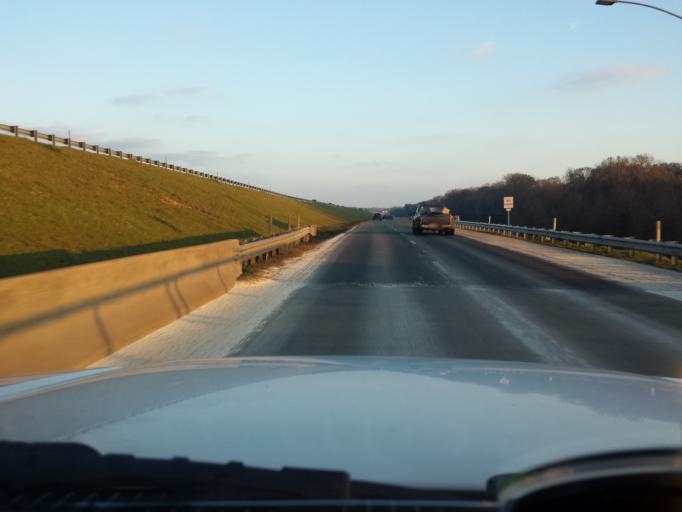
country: US
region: Mississippi
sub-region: Madison County
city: Ridgeland
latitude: 32.3965
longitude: -90.0635
